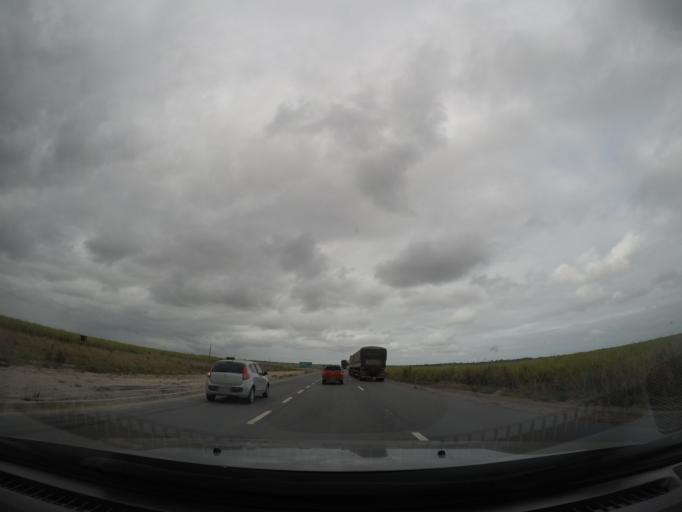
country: BR
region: Alagoas
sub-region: Pilar
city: Pilar
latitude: -9.6740
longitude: -36.0323
